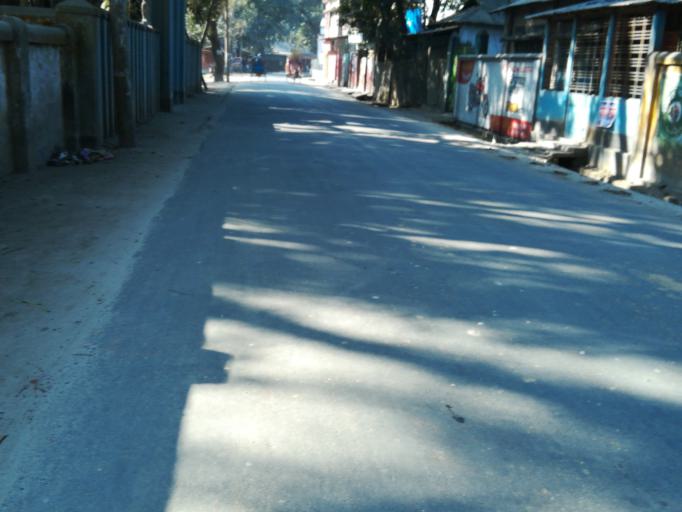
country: BD
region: Rangpur Division
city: Nageswari
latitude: 25.8146
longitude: 89.6470
